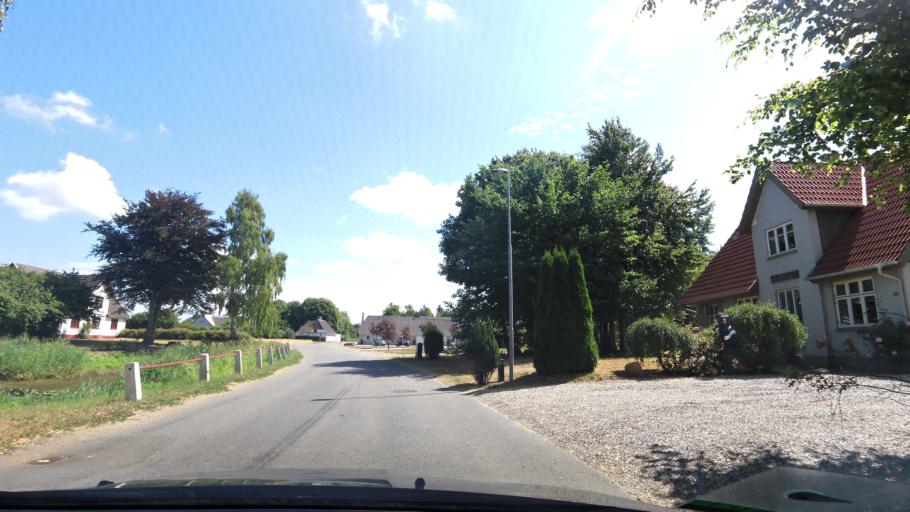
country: DK
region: South Denmark
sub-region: Nordfyns Kommune
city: Otterup
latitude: 55.5493
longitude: 10.4464
